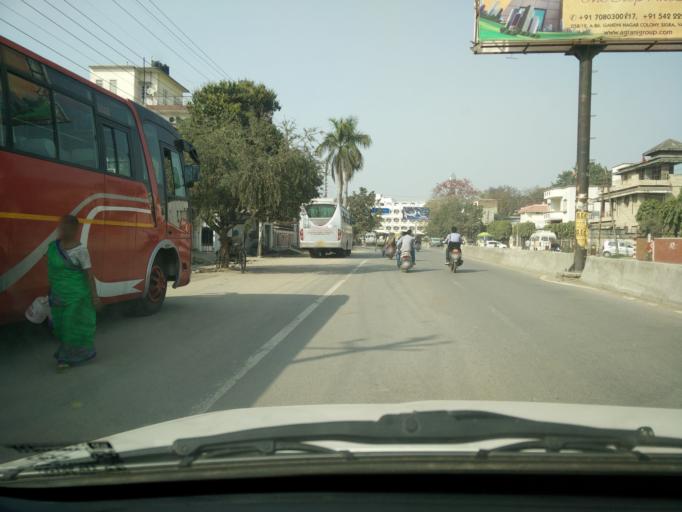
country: IN
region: Uttar Pradesh
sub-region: Varanasi
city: Varanasi
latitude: 25.2947
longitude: 83.0024
